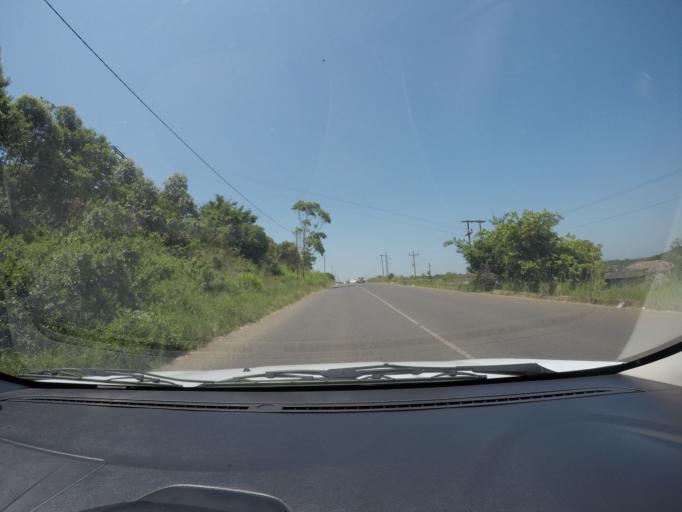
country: ZA
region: KwaZulu-Natal
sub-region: uThungulu District Municipality
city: eSikhawini
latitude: -28.8522
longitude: 31.9242
